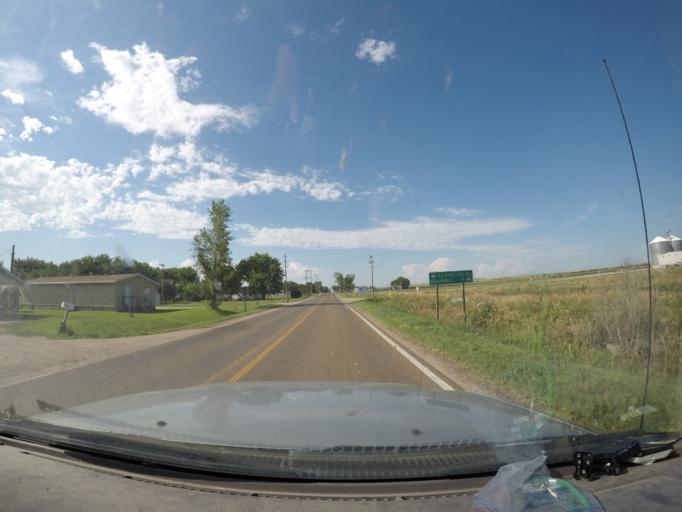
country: US
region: Nebraska
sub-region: Buffalo County
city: Kearney
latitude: 40.7002
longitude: -99.2553
